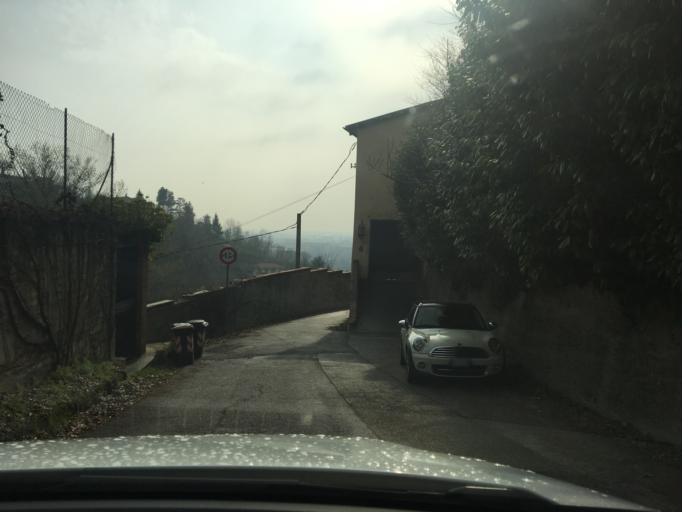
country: IT
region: Piedmont
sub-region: Provincia di Torino
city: Moncalieri
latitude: 45.0290
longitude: 7.6820
